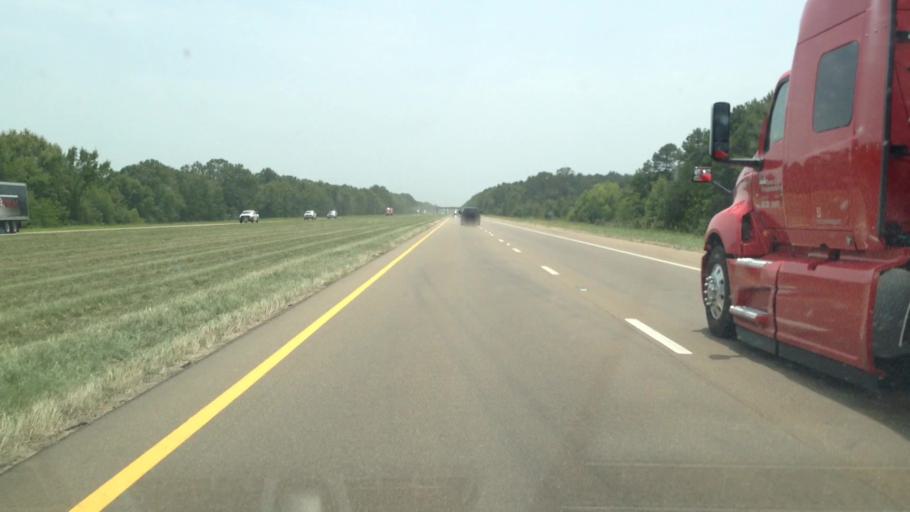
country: US
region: Texas
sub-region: Morris County
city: Naples
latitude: 33.3423
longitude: -94.6607
